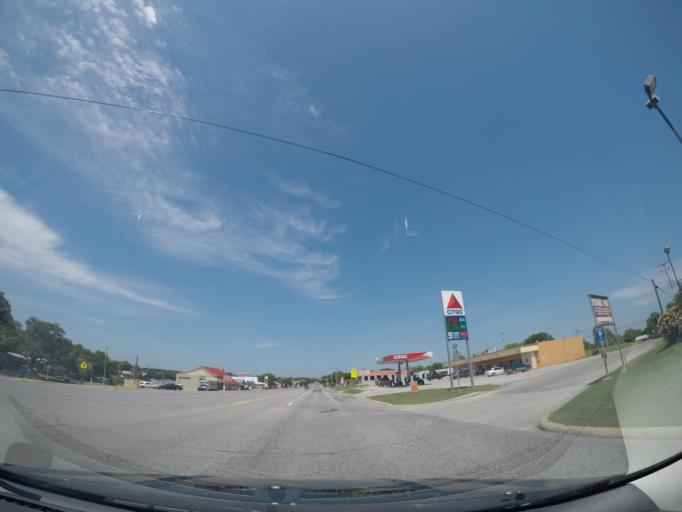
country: US
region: Texas
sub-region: Medina County
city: Castroville
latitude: 29.3518
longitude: -98.8849
